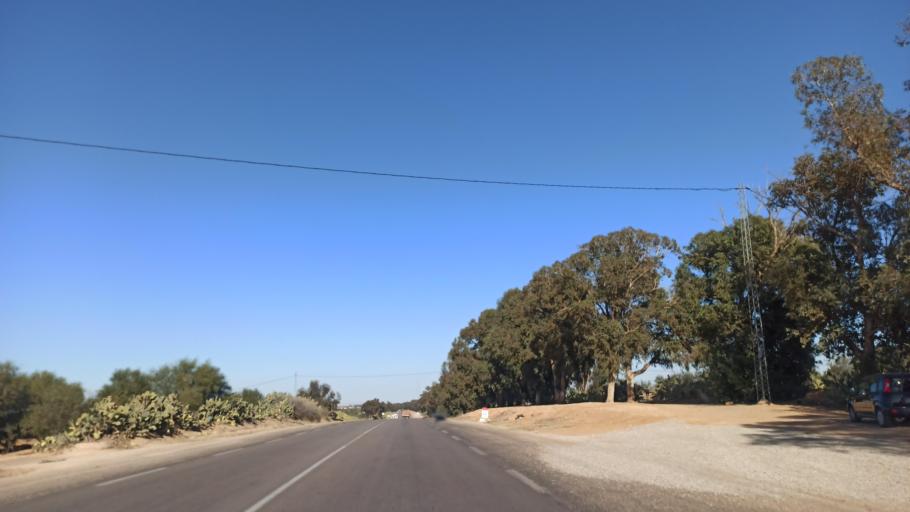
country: TN
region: Sidi Bu Zayd
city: Jilma
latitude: 35.1658
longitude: 9.3688
